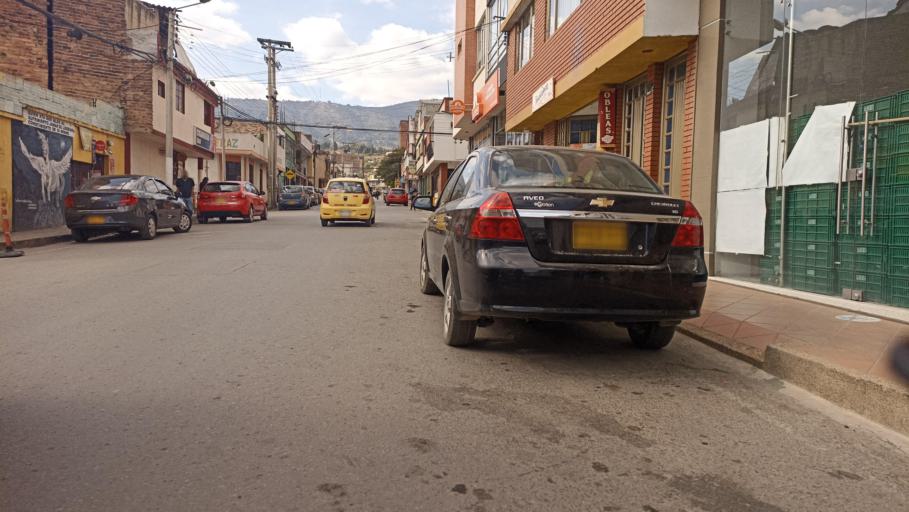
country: CO
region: Boyaca
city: Duitama
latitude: 5.8316
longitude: -73.0346
